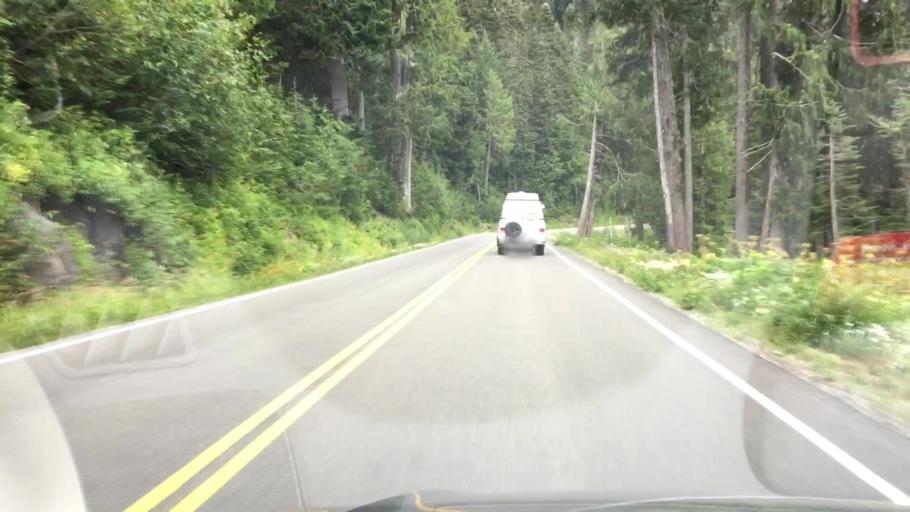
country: US
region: Washington
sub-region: Pierce County
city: Buckley
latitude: 46.7783
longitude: -121.7447
